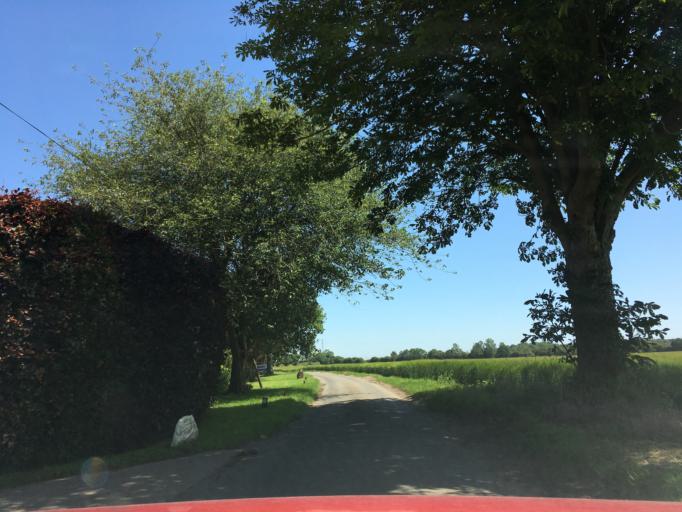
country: GB
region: England
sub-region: Northamptonshire
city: Brackley
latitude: 51.9954
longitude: -1.1066
